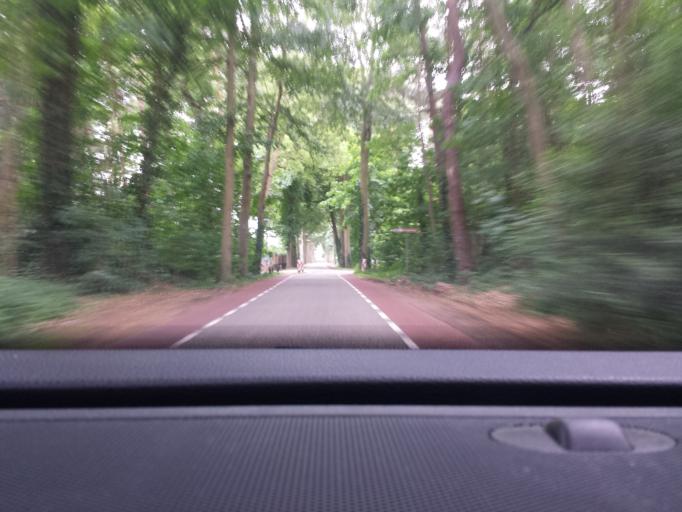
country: NL
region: Gelderland
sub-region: Gemeente Bronckhorst
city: Zelhem
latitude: 52.0120
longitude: 6.3443
